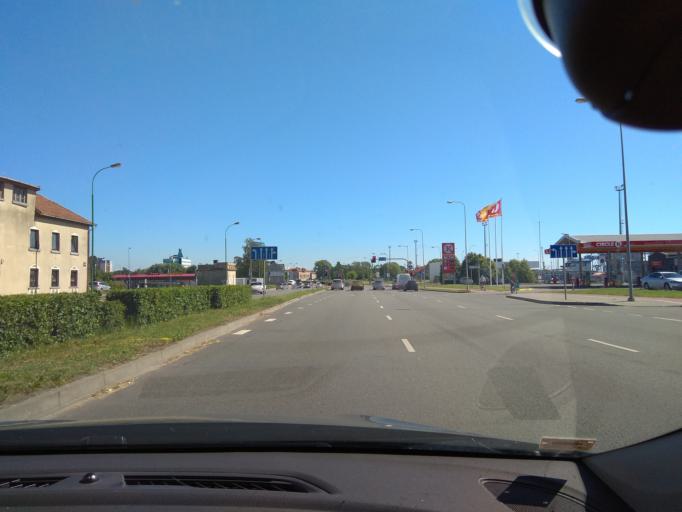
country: LT
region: Klaipedos apskritis
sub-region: Klaipeda
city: Klaipeda
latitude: 55.6884
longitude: 21.1452
